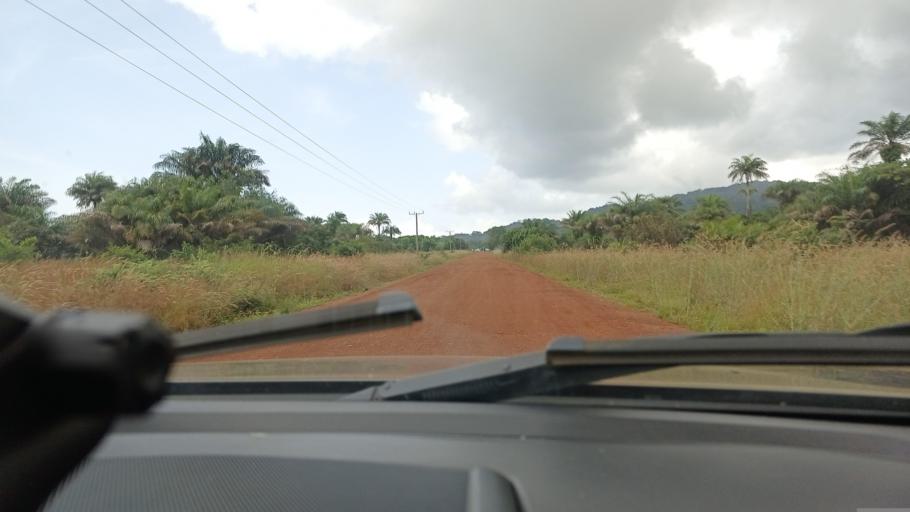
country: LR
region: Grand Cape Mount
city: Robertsport
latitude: 6.7042
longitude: -11.3256
